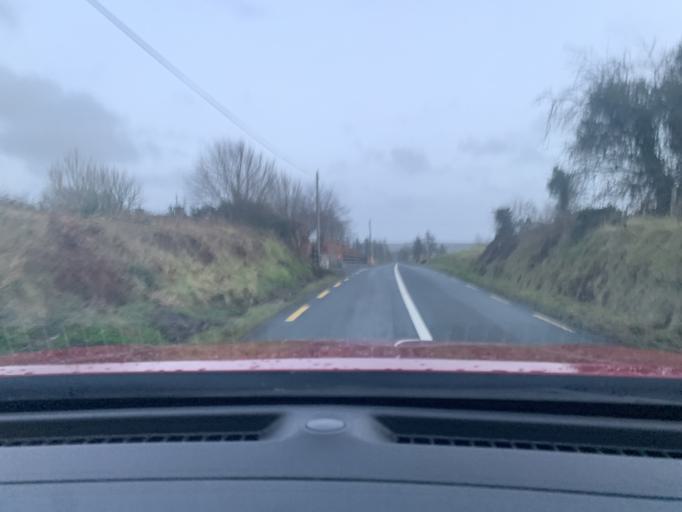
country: IE
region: Connaught
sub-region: Sligo
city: Ballymote
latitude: 54.0341
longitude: -8.4190
